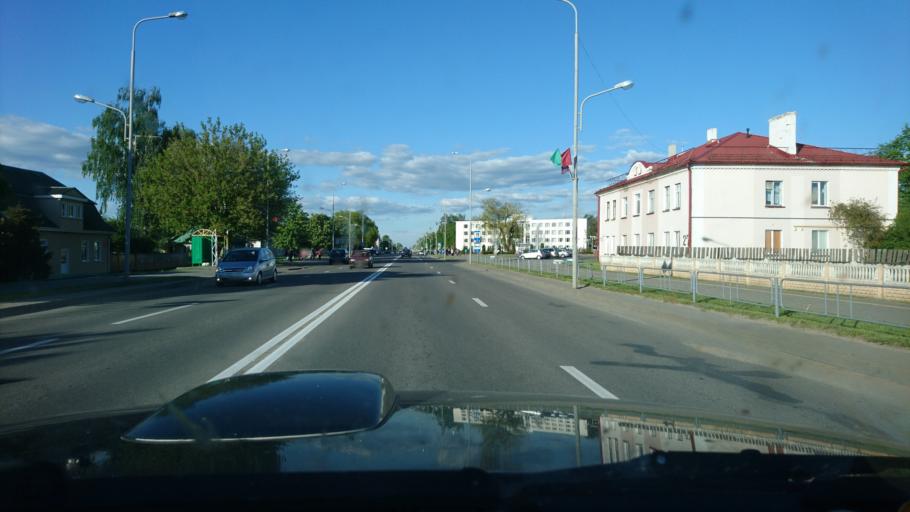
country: BY
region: Brest
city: Ivatsevichy
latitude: 52.7083
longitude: 25.3358
